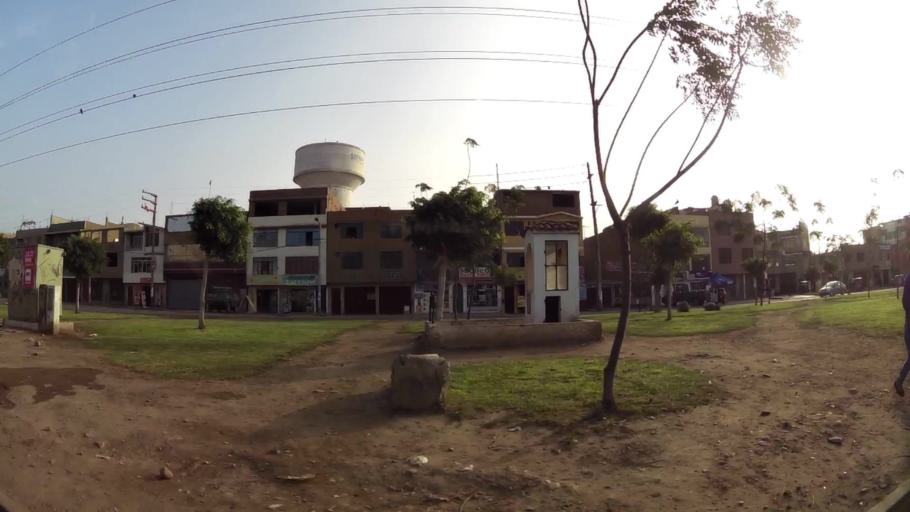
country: PE
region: Lima
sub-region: Lima
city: Independencia
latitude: -12.0000
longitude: -77.1021
